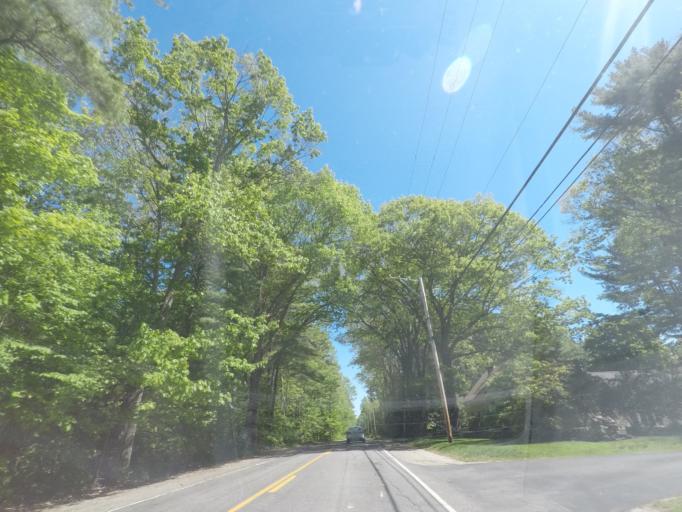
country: US
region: Maine
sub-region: Kennebec County
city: Manchester
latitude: 44.2981
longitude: -69.8869
